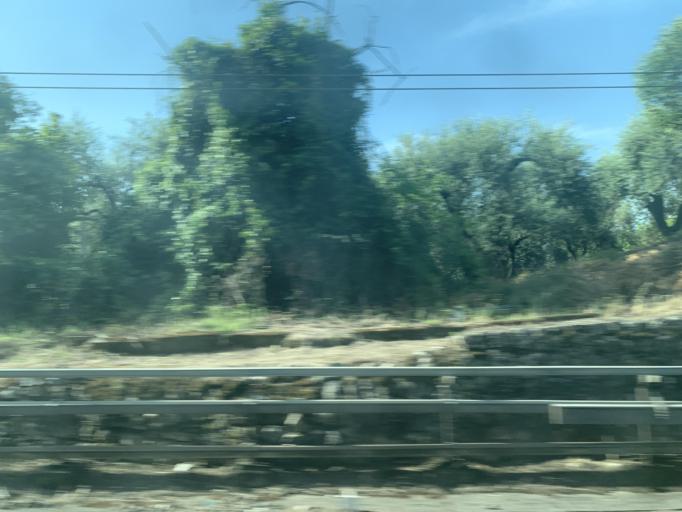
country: IT
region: Latium
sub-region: Provincia di Latina
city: Gaeta
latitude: 41.2547
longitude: 13.5898
